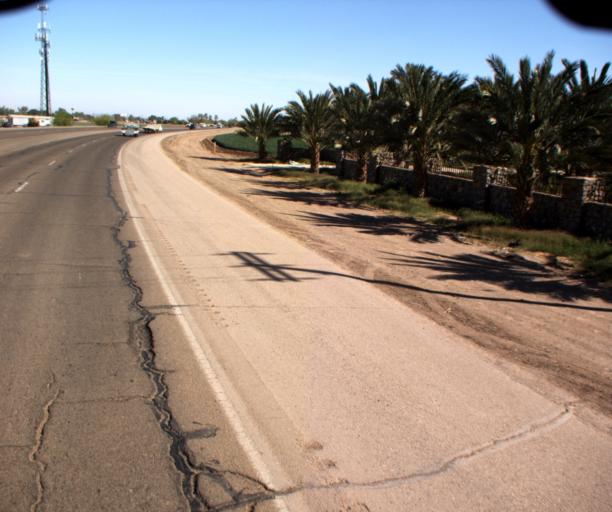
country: US
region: Arizona
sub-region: Yuma County
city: San Luis
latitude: 32.5463
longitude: -114.7868
